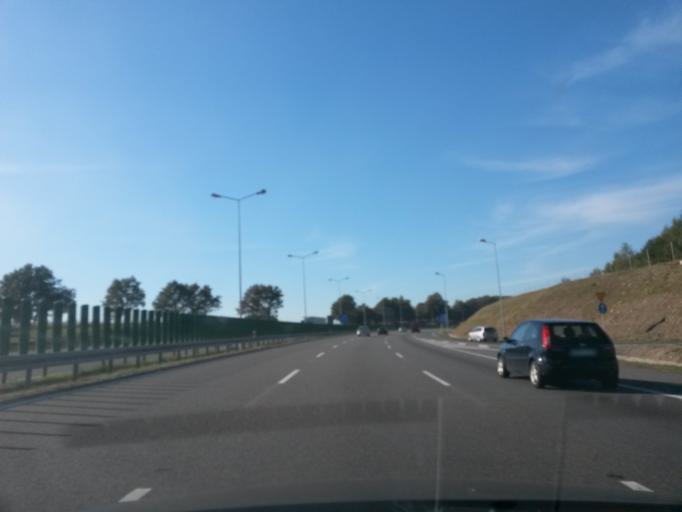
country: PL
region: Opole Voivodeship
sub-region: Powiat strzelecki
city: Lesnica
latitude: 50.4624
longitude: 18.1585
